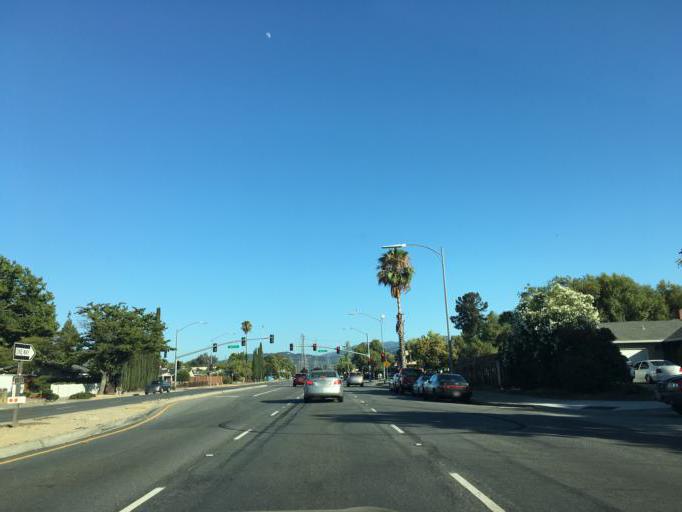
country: US
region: California
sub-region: Santa Clara County
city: Cambrian Park
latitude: 37.2437
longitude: -121.9065
